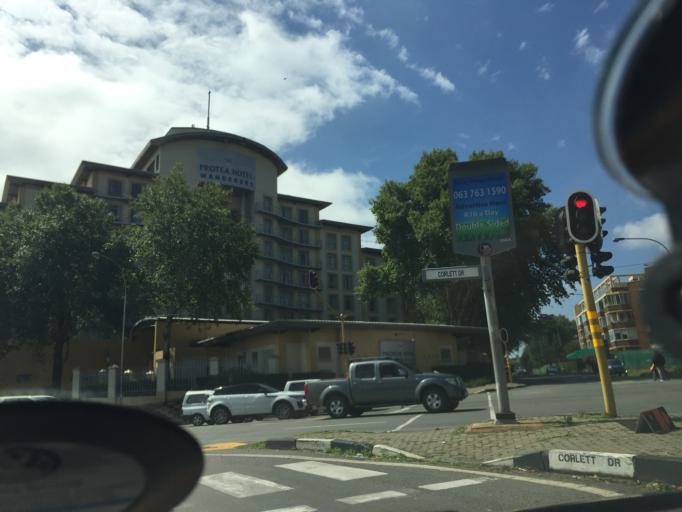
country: ZA
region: Gauteng
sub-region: City of Johannesburg Metropolitan Municipality
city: Johannesburg
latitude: -26.1339
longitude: 28.0520
